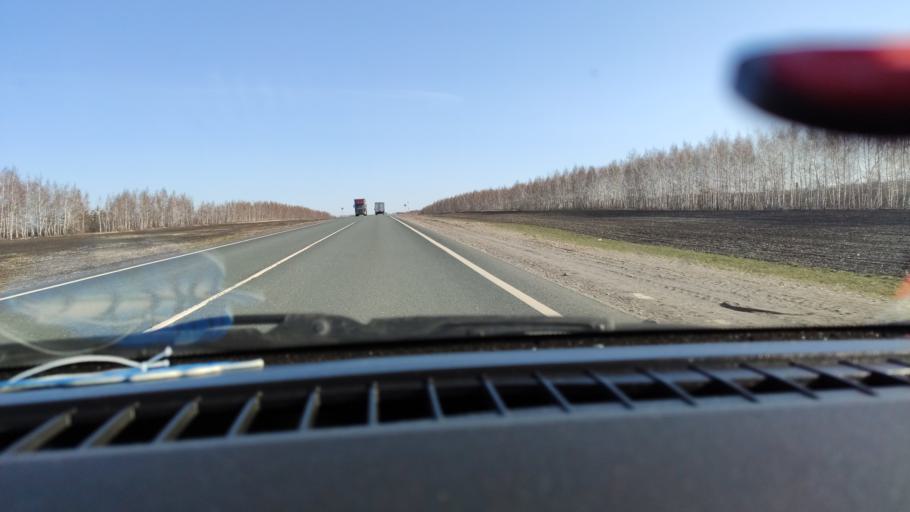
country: RU
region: Samara
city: Syzran'
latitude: 52.9058
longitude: 48.2982
